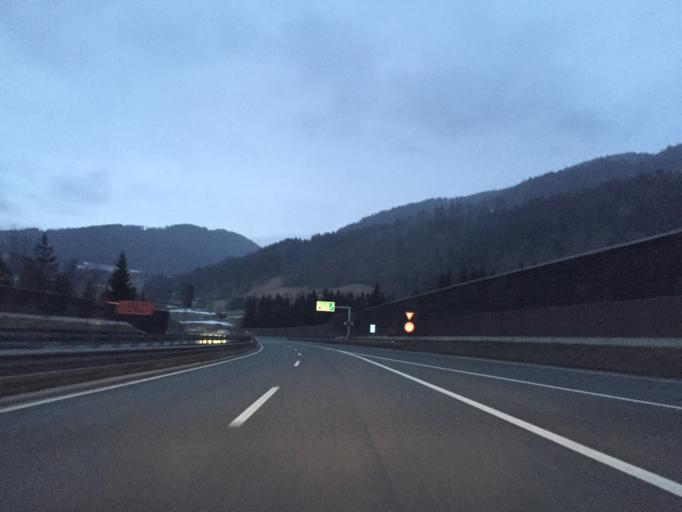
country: AT
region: Salzburg
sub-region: Politischer Bezirk Sankt Johann im Pongau
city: Eben im Pongau
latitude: 47.4160
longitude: 13.3880
